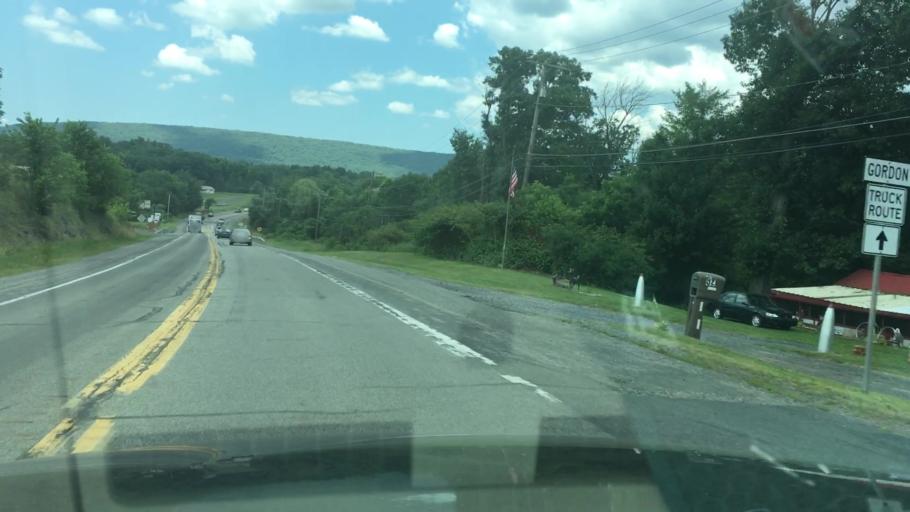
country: US
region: Pennsylvania
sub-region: Schuylkill County
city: Ashland
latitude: 40.7384
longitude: -76.3887
